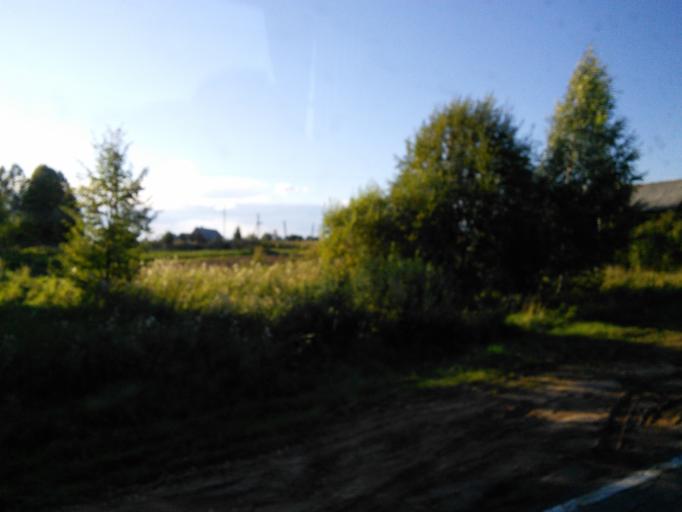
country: RU
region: Jaroslavl
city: Poshekhon'ye
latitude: 58.4578
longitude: 39.0395
